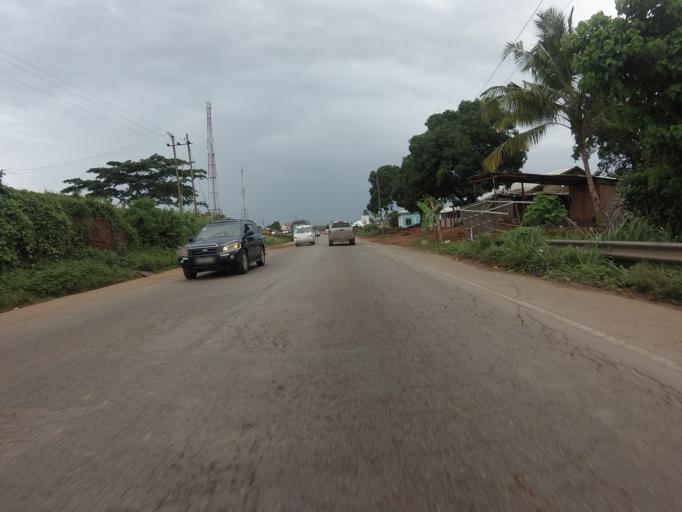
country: GH
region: Ashanti
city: Konongo
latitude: 6.6244
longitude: -1.2046
